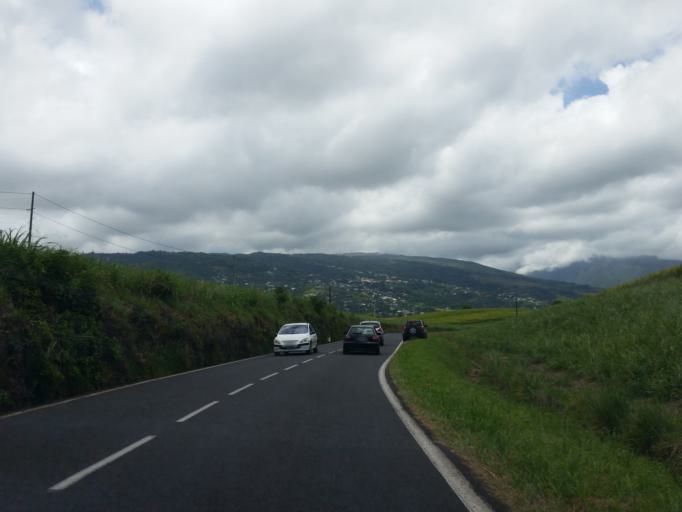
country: RE
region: Reunion
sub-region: Reunion
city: Sainte-Marie
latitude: -20.9210
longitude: 55.5405
